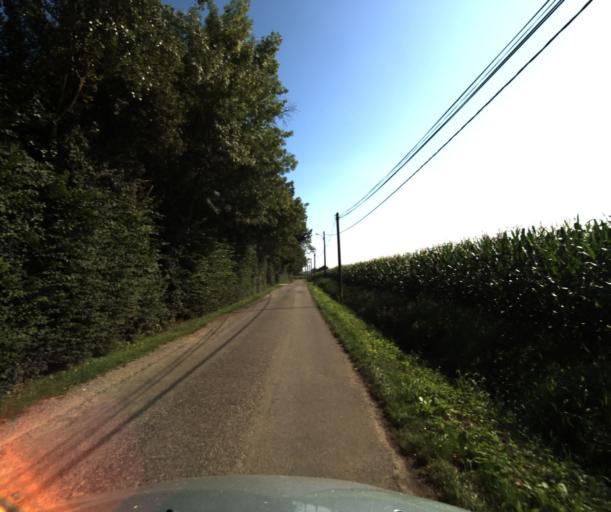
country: FR
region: Midi-Pyrenees
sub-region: Departement de la Haute-Garonne
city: Le Fauga
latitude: 43.4141
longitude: 1.3052
